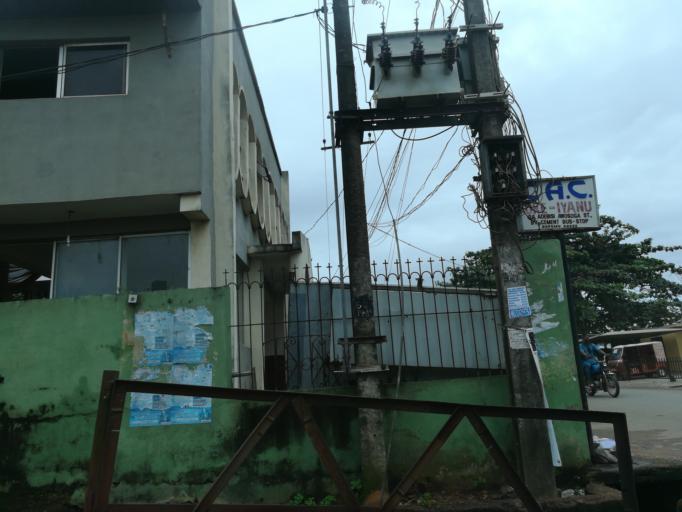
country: NG
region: Lagos
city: Agege
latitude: 6.6107
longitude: 3.3177
